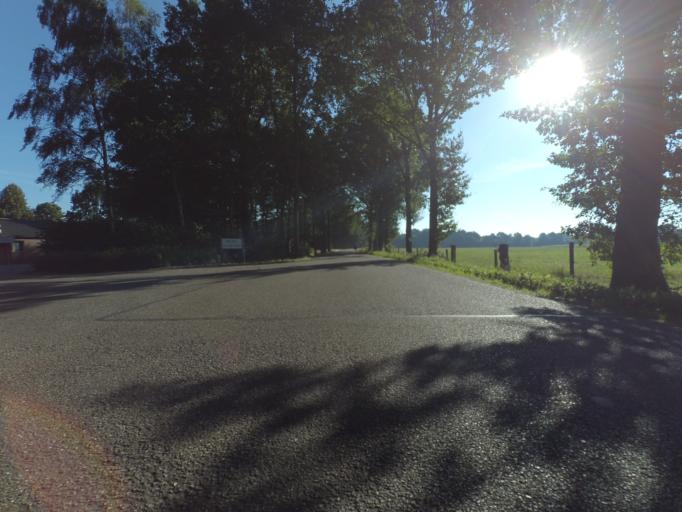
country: NL
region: Gelderland
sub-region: Gemeente Putten
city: Putten
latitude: 52.2478
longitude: 5.5920
